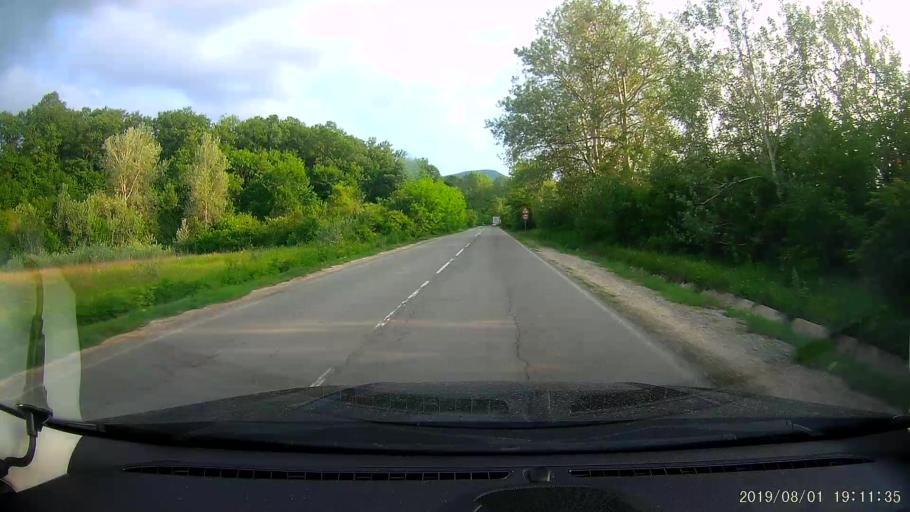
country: BG
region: Shumen
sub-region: Obshtina Smyadovo
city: Smyadovo
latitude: 42.9723
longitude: 26.9598
